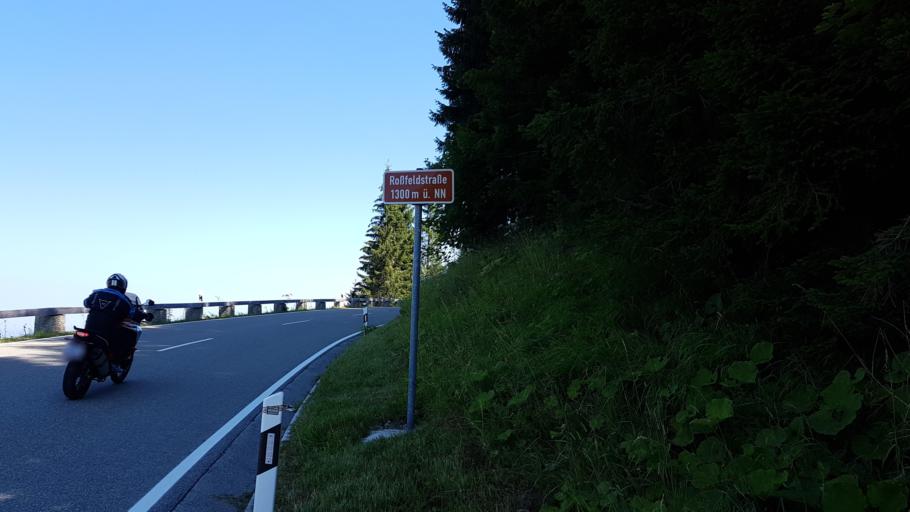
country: AT
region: Salzburg
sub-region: Politischer Bezirk Hallein
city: Hallein
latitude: 47.6230
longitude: 13.0714
